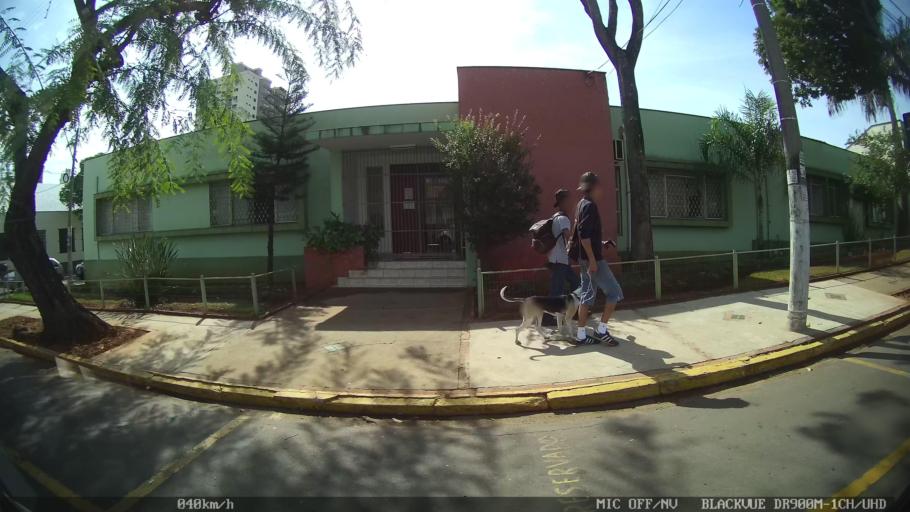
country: BR
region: Sao Paulo
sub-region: Piracicaba
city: Piracicaba
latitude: -22.7376
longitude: -47.6499
